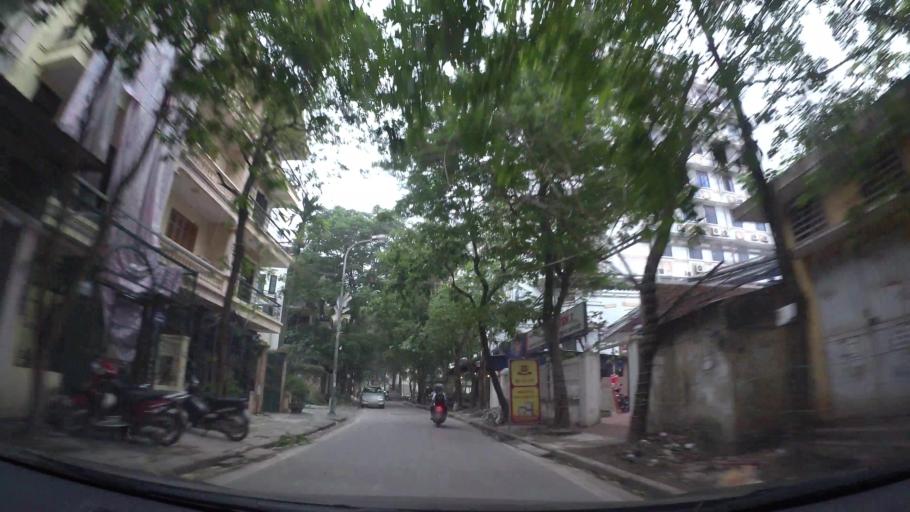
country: VN
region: Ha Noi
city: Thanh Xuan
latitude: 20.9850
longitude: 105.8297
